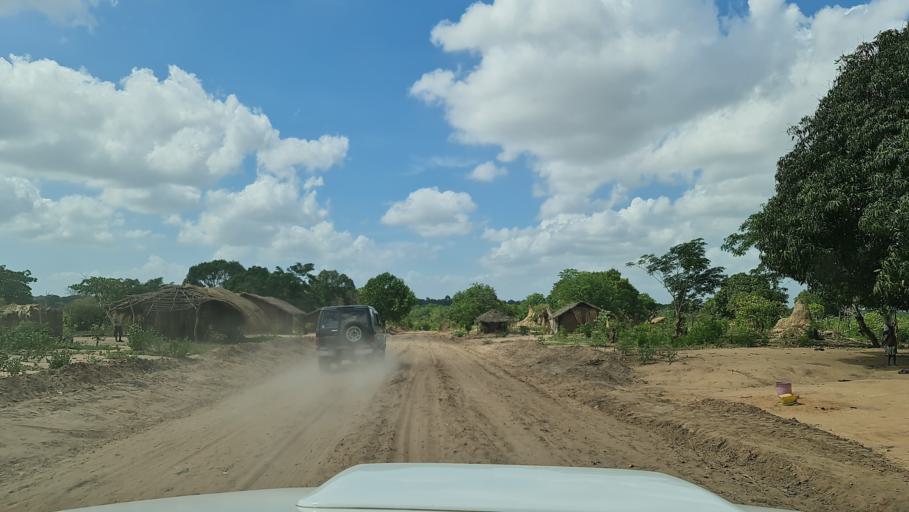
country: MZ
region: Nampula
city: Ilha de Mocambique
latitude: -15.0092
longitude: 40.5609
